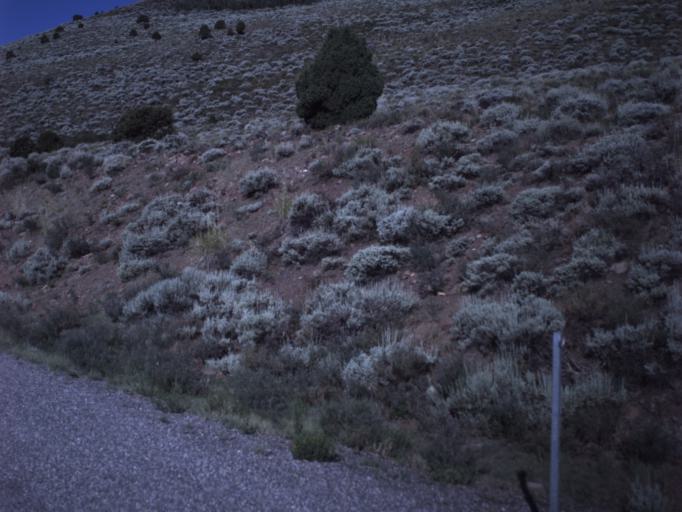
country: US
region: Utah
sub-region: Wayne County
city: Loa
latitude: 38.5929
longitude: -111.4716
